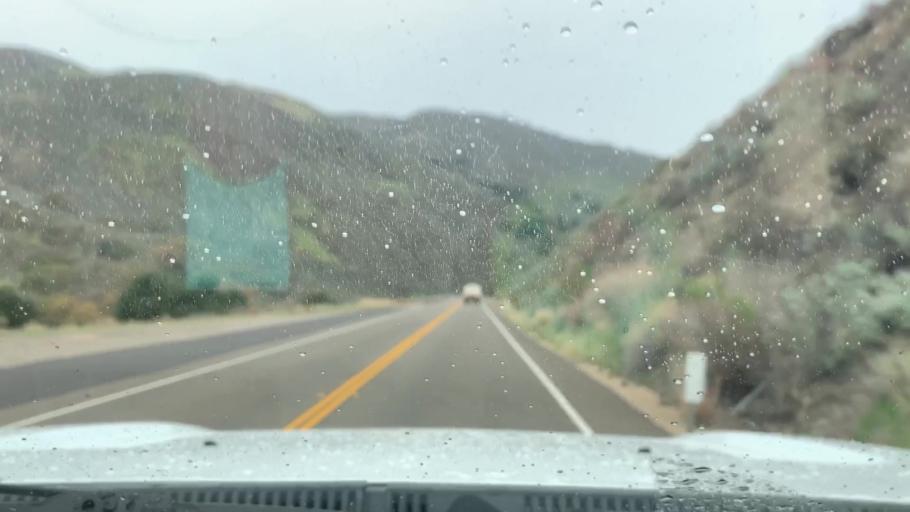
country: US
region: California
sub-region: Santa Barbara County
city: Santa Maria
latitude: 35.0461
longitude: -120.1828
